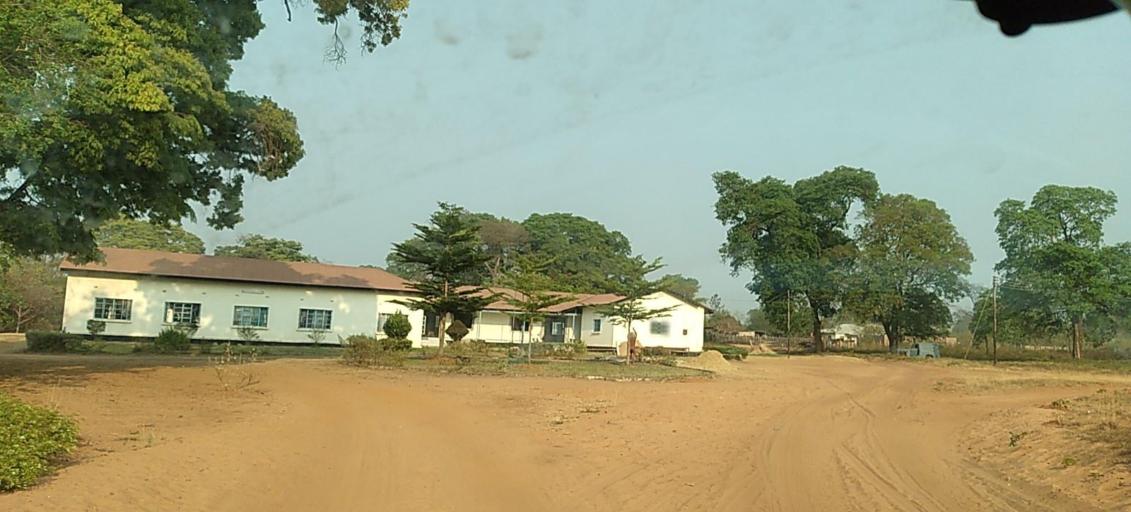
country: ZM
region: North-Western
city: Kabompo
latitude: -13.5994
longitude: 24.2070
